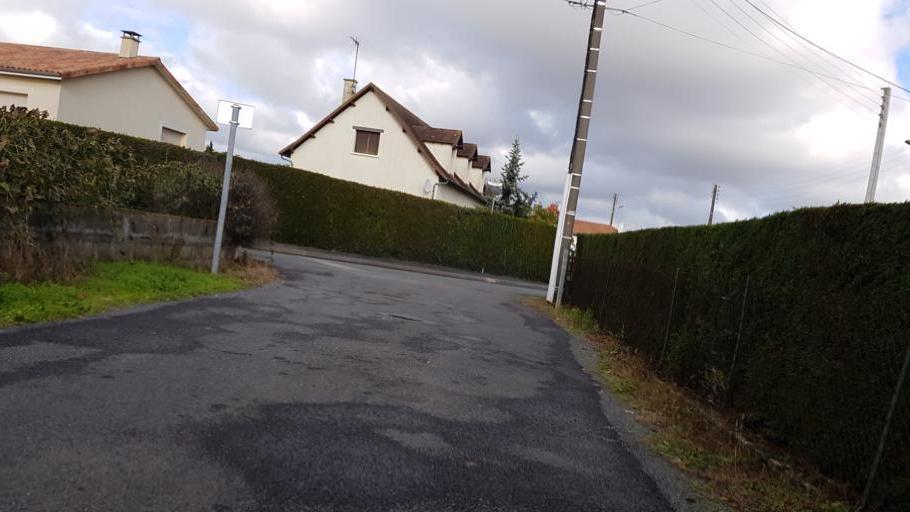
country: FR
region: Poitou-Charentes
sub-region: Departement de la Vienne
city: Chasseneuil-du-Poitou
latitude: 46.6491
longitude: 0.3704
